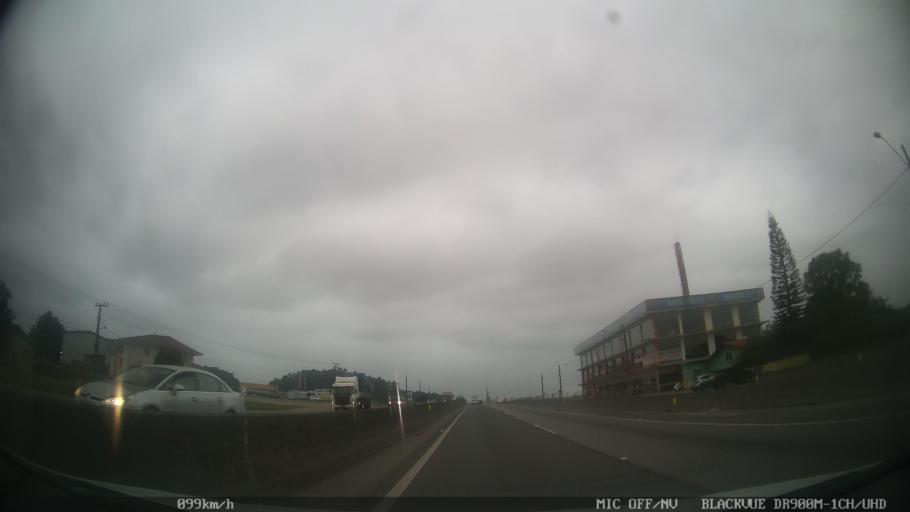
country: BR
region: Santa Catarina
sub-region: Barra Velha
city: Barra Velha
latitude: -26.6282
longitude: -48.7080
